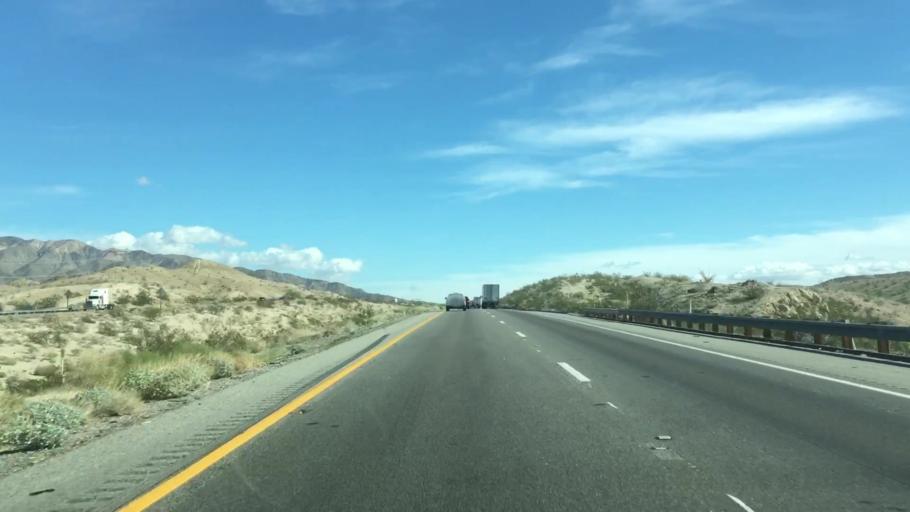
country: US
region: California
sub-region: Riverside County
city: Mecca
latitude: 33.6791
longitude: -115.9928
